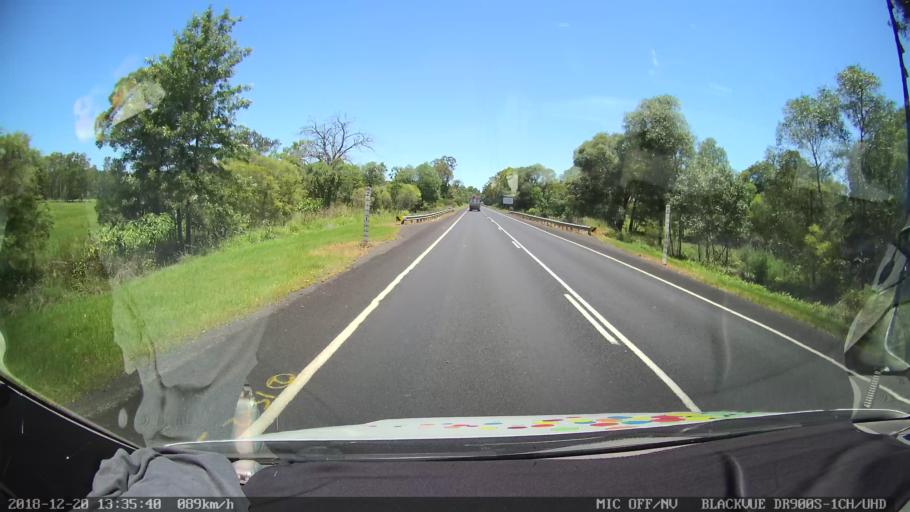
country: AU
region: New South Wales
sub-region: Clarence Valley
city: Gordon
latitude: -29.2723
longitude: 152.9921
